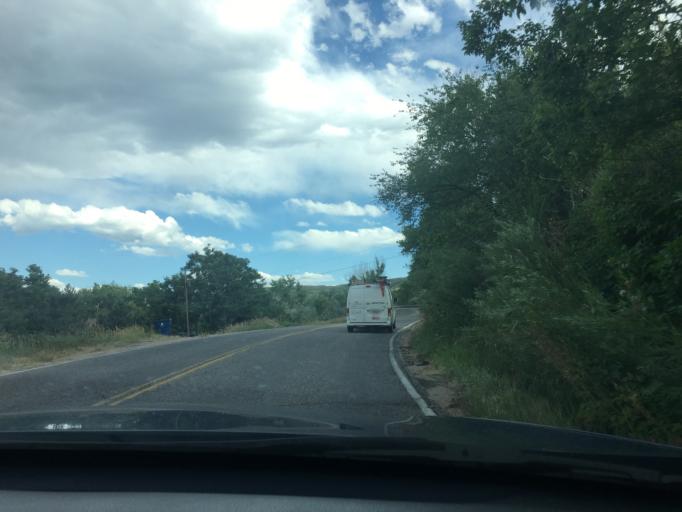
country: US
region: Colorado
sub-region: Jefferson County
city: Applewood
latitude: 39.7655
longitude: -105.1830
